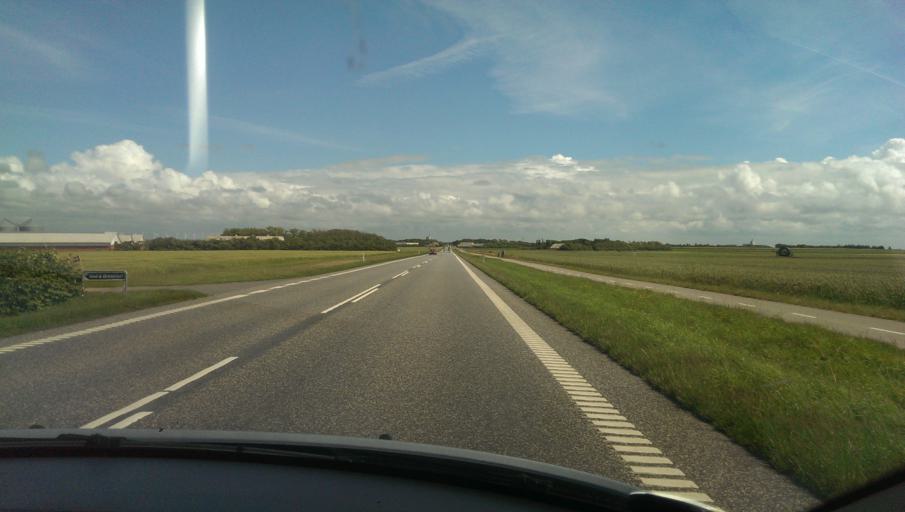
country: DK
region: Central Jutland
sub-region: Ringkobing-Skjern Kommune
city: Ringkobing
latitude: 56.1110
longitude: 8.1927
